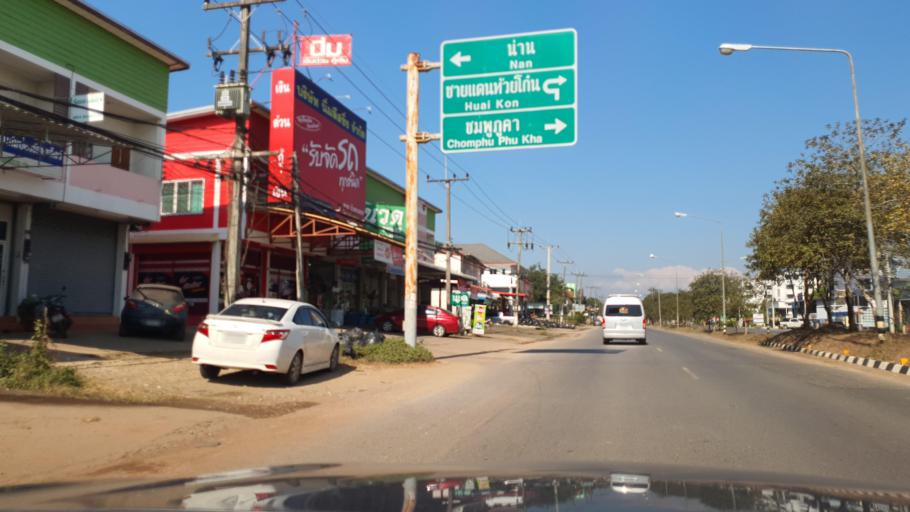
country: TH
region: Nan
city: Pua
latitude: 19.1695
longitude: 100.9217
